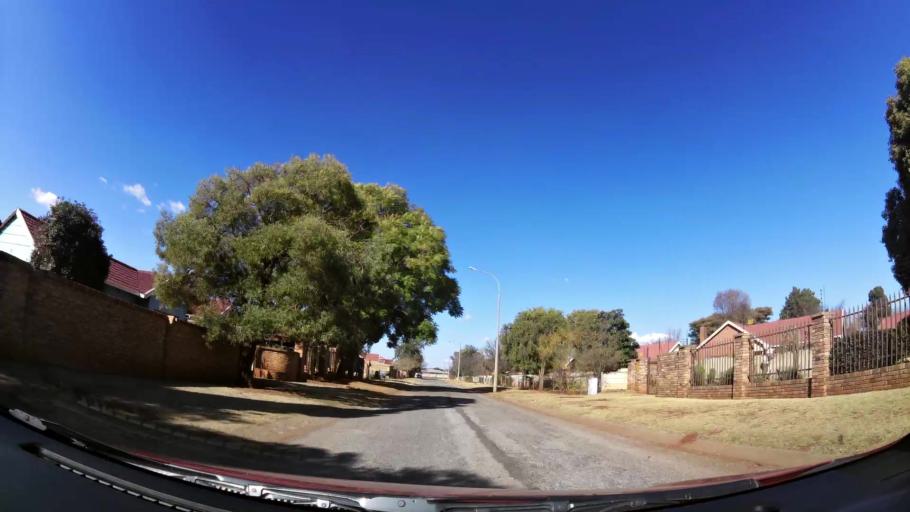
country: ZA
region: Gauteng
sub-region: West Rand District Municipality
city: Carletonville
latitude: -26.3592
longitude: 27.3712
